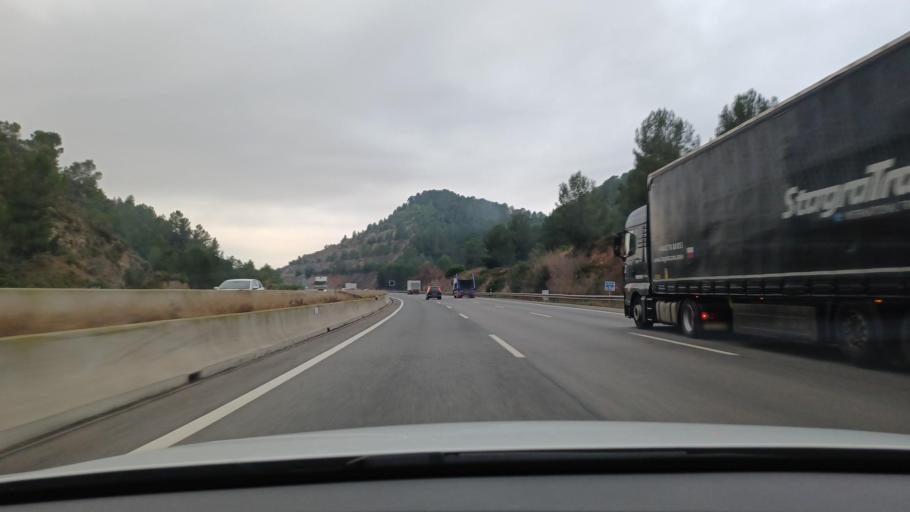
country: ES
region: Valencia
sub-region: Provincia de Valencia
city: Llosa de Ranes
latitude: 39.0420
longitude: -0.5520
